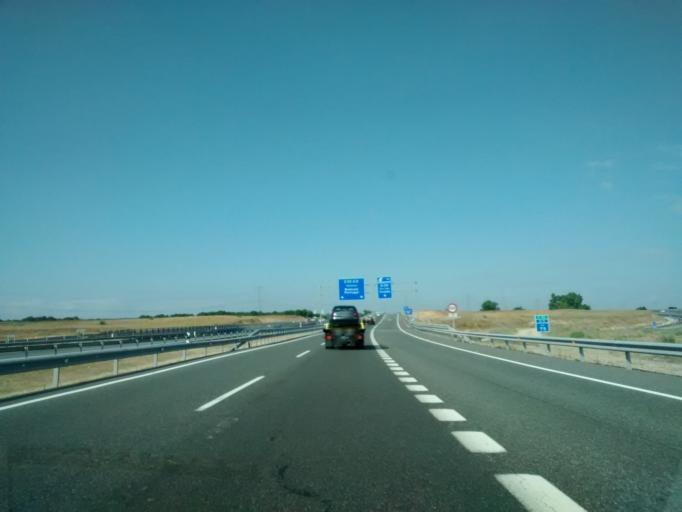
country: ES
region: Castille-La Mancha
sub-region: Province of Toledo
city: Maqueda
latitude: 40.0552
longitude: -4.3778
